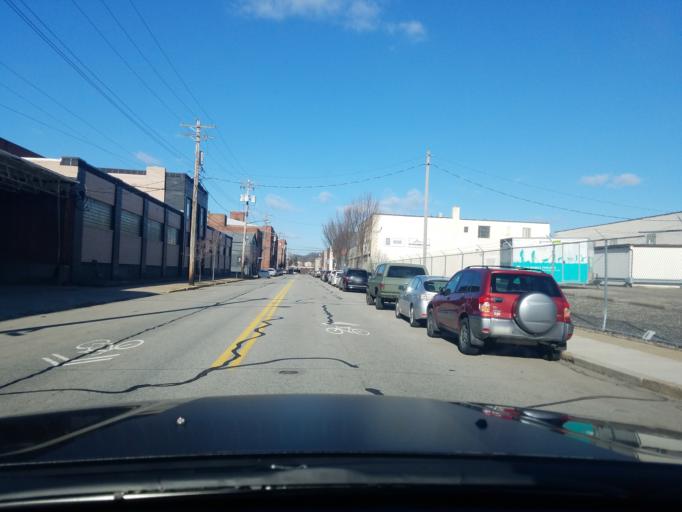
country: US
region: Pennsylvania
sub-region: Allegheny County
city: Aspinwall
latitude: 40.4584
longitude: -79.9121
